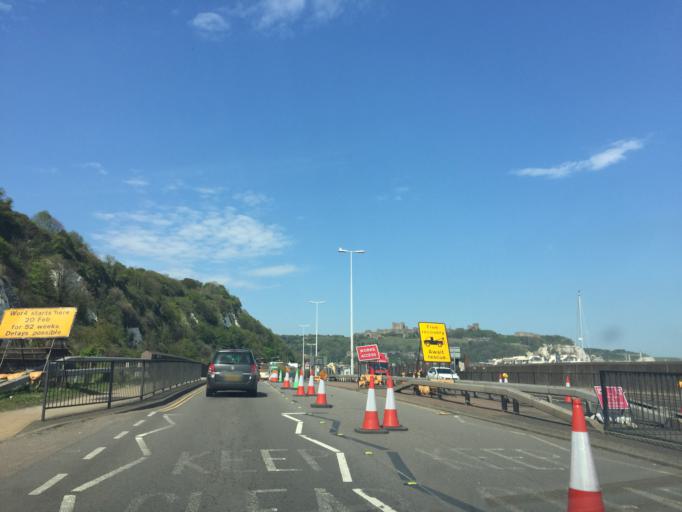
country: GB
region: England
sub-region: Kent
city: Dover
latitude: 51.1183
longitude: 1.3077
